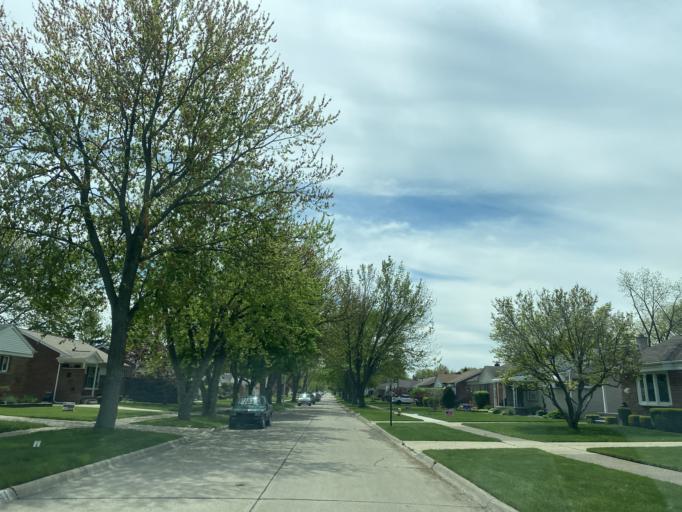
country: US
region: Michigan
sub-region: Wayne County
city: Riverview
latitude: 42.1772
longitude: -83.1863
